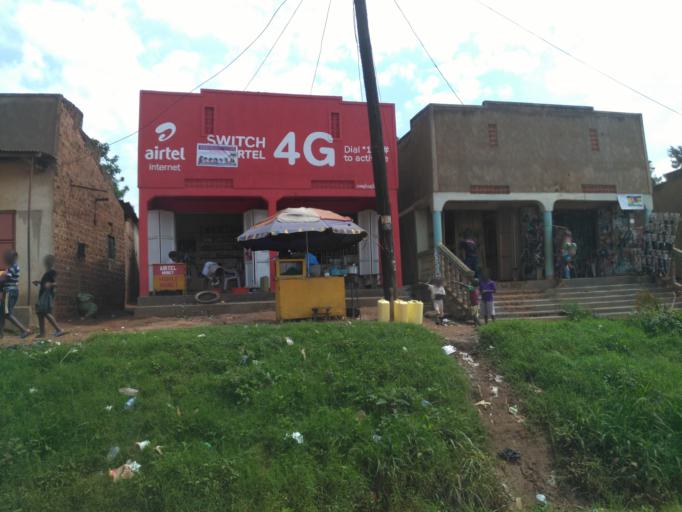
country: UG
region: Central Region
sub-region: Wakiso District
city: Kireka
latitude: 0.4533
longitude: 32.6071
